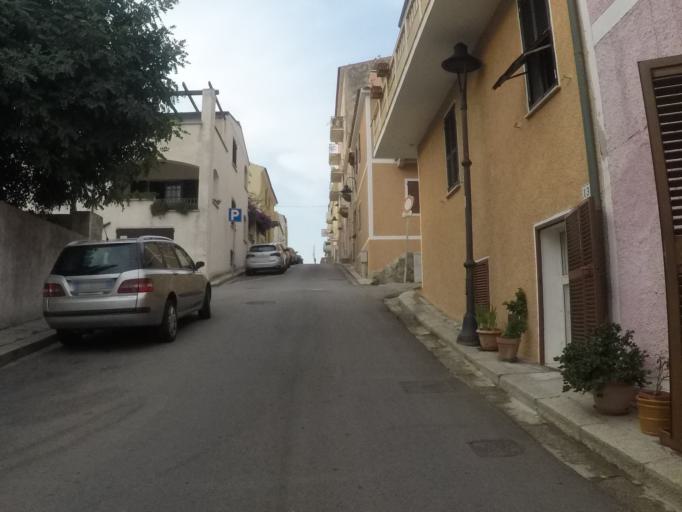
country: IT
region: Sardinia
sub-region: Provincia di Olbia-Tempio
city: Santa Teresa Gallura
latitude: 41.2434
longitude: 9.1907
